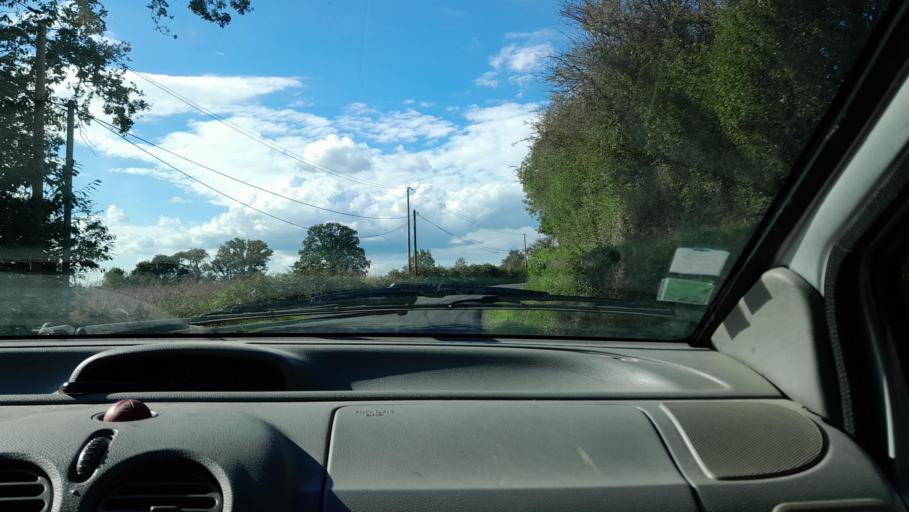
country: FR
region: Pays de la Loire
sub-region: Departement de la Mayenne
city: Ahuille
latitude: 48.0196
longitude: -0.8764
